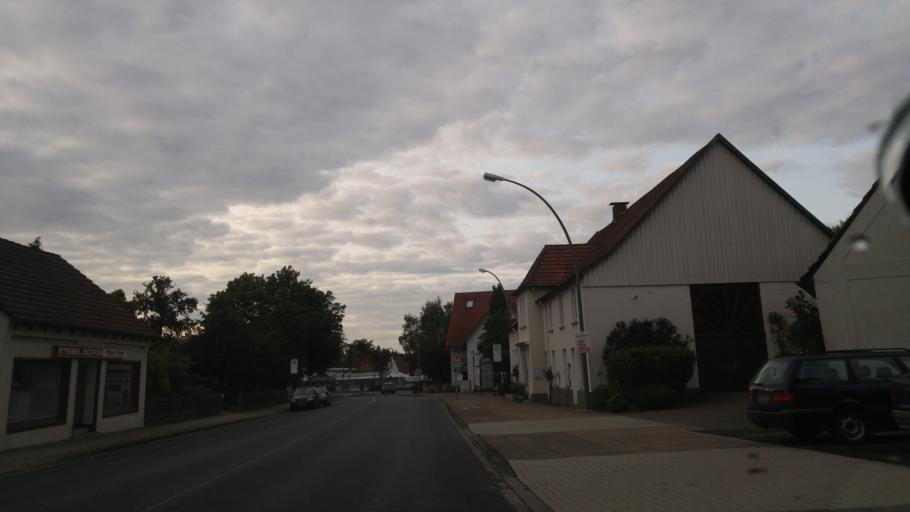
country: DE
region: North Rhine-Westphalia
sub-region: Regierungsbezirk Detmold
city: Bielefeld
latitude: 52.0552
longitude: 8.5478
